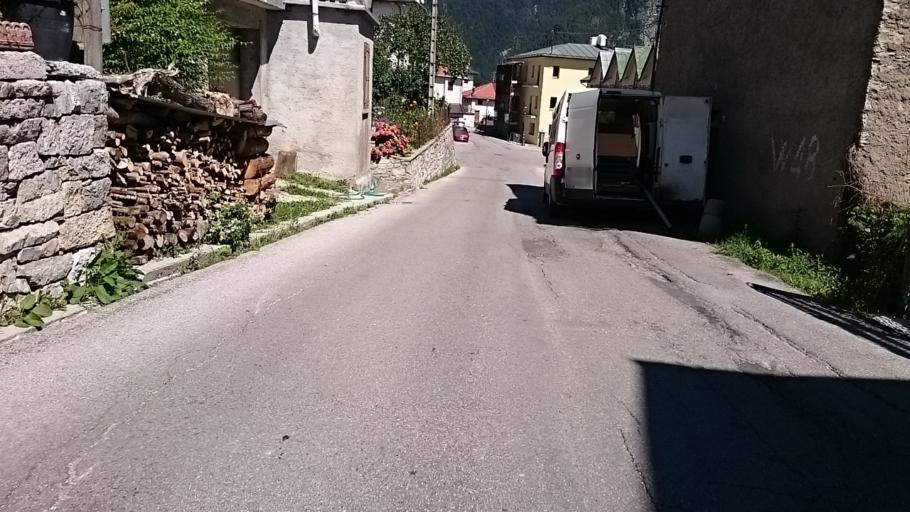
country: IT
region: Veneto
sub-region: Provincia di Belluno
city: Pieve di Cadore
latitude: 46.4232
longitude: 12.3768
